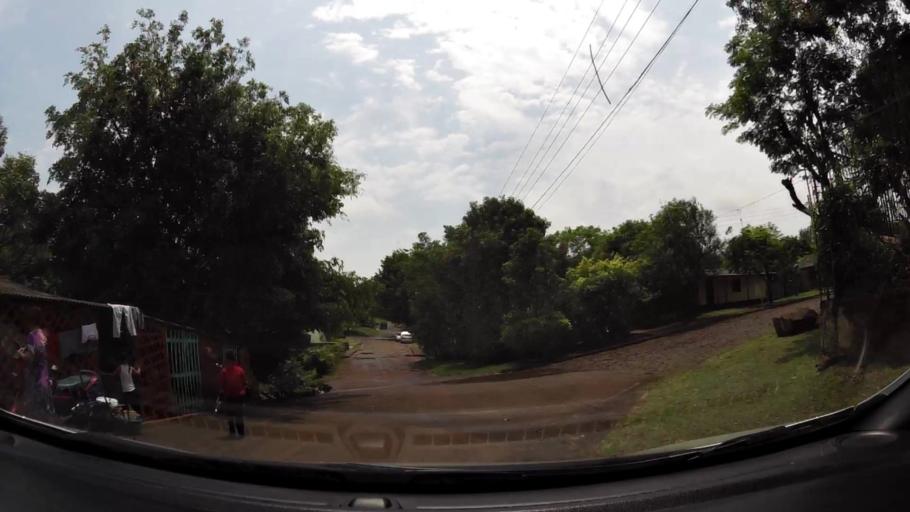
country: PY
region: Alto Parana
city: Ciudad del Este
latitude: -25.5060
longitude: -54.6556
